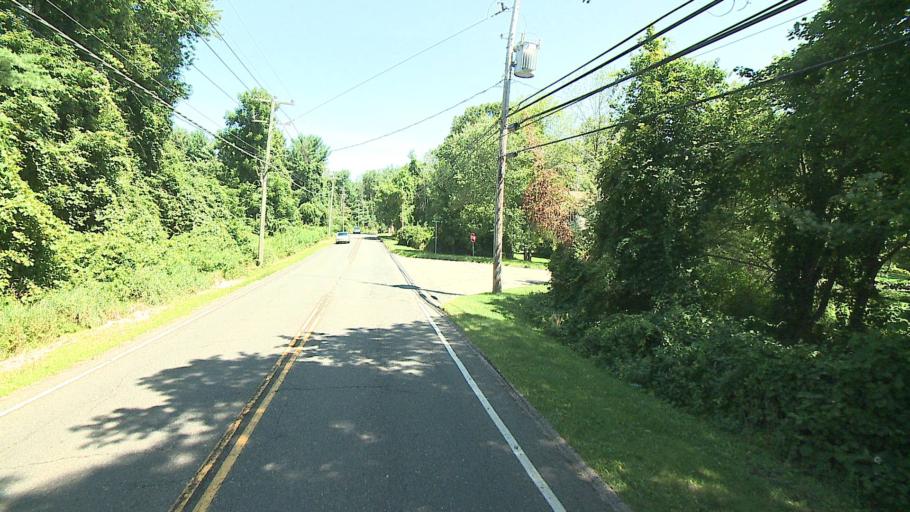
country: US
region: Connecticut
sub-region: Fairfield County
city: Trumbull
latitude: 41.3413
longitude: -73.2030
